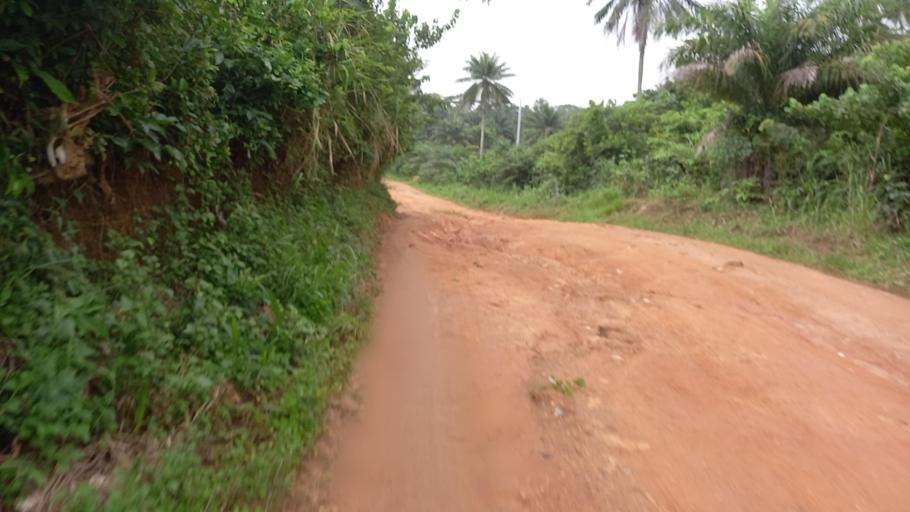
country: SL
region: Eastern Province
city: Kailahun
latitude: 8.2438
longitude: -10.5181
